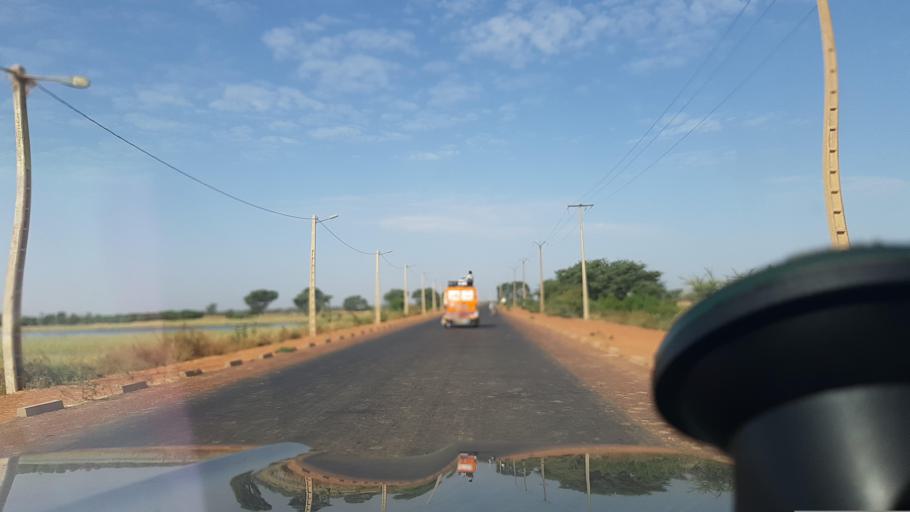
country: ML
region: Segou
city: Markala
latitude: 13.6848
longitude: -6.0950
